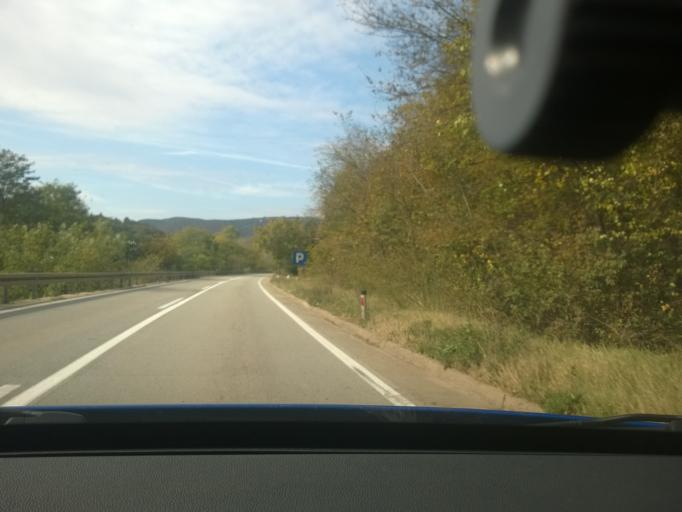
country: RS
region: Central Serbia
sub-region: Nisavski Okrug
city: Niska Banja
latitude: 43.3328
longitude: 22.0746
